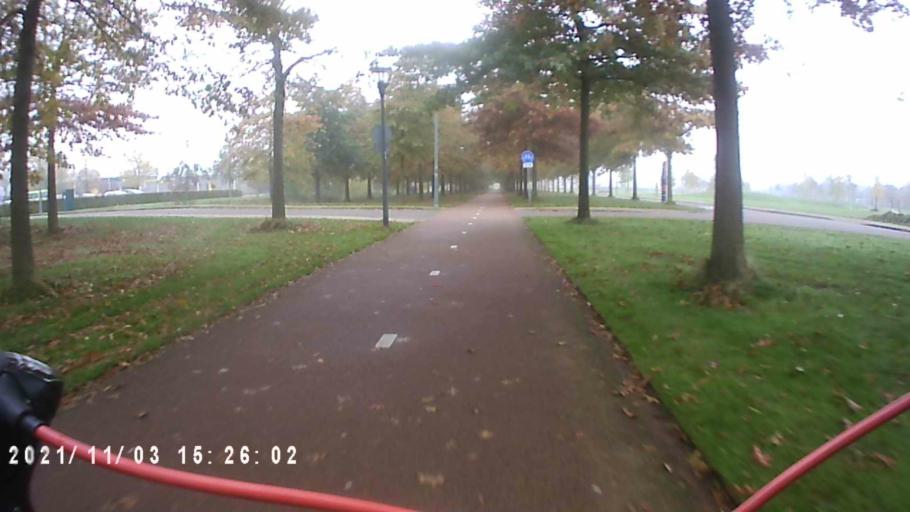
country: NL
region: Groningen
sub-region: Gemeente Leek
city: Leek
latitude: 53.1455
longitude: 6.3740
